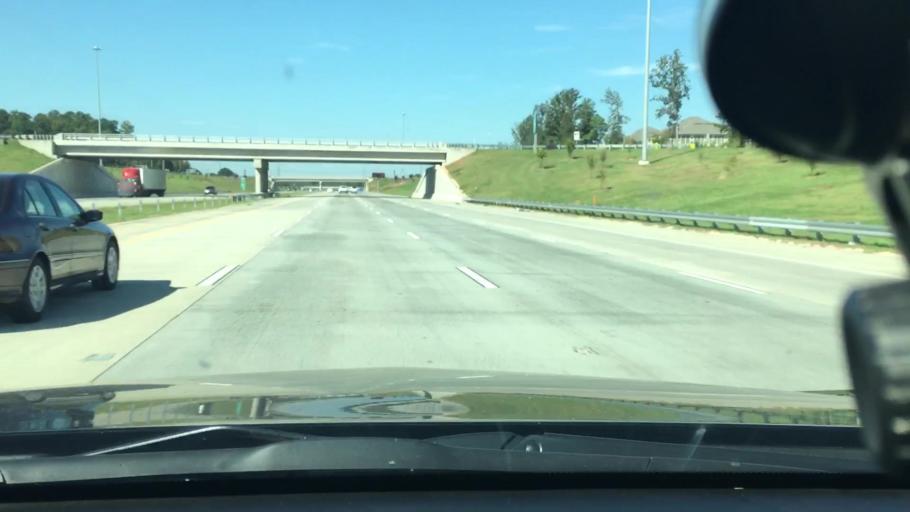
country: US
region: North Carolina
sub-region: Mecklenburg County
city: Huntersville
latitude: 35.3688
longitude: -80.7786
